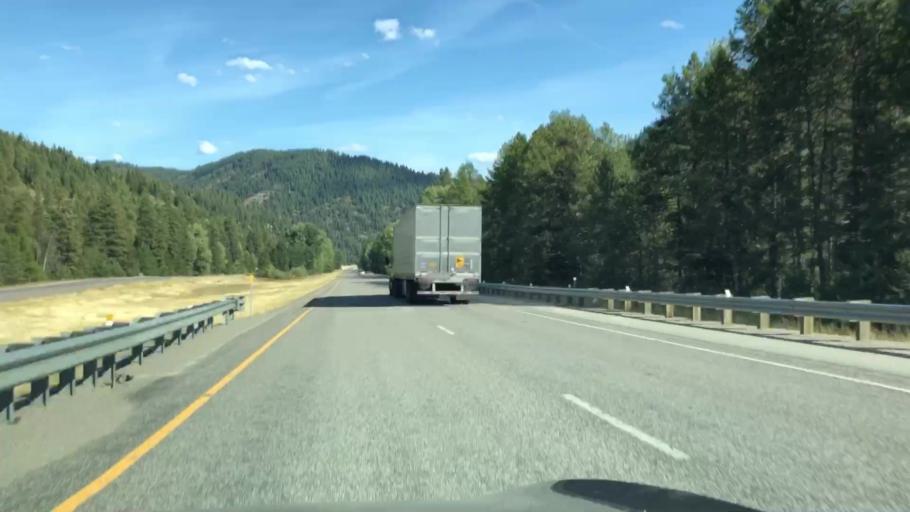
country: US
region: Montana
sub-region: Sanders County
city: Thompson Falls
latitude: 47.3595
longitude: -115.3151
